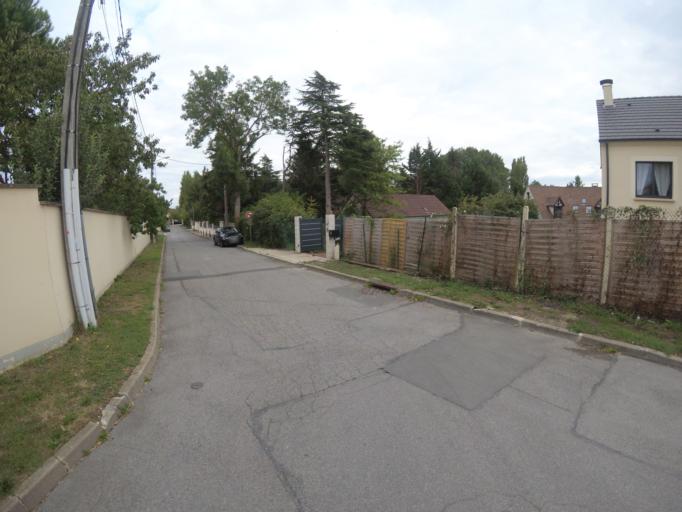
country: FR
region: Ile-de-France
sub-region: Departement de Seine-et-Marne
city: Lagny-sur-Marne
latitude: 48.8628
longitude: 2.7151
